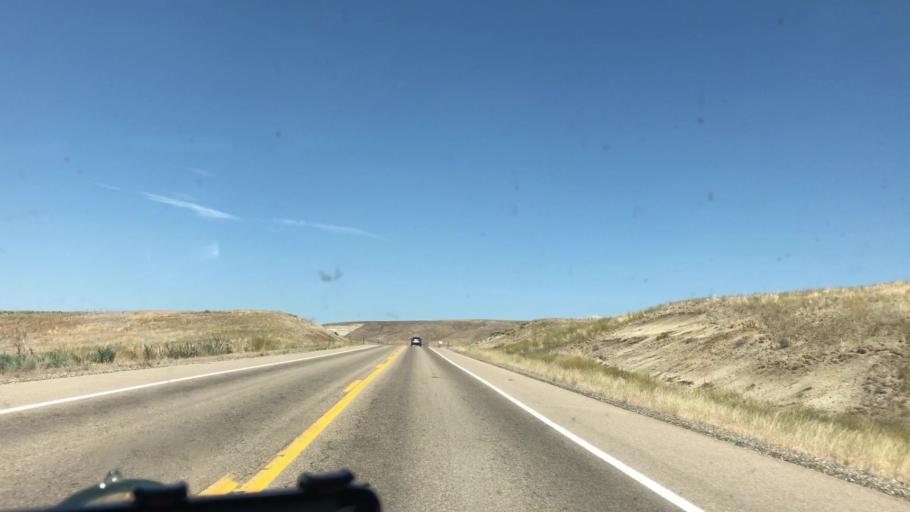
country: US
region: Idaho
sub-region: Owyhee County
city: Marsing
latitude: 43.2753
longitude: -116.9984
